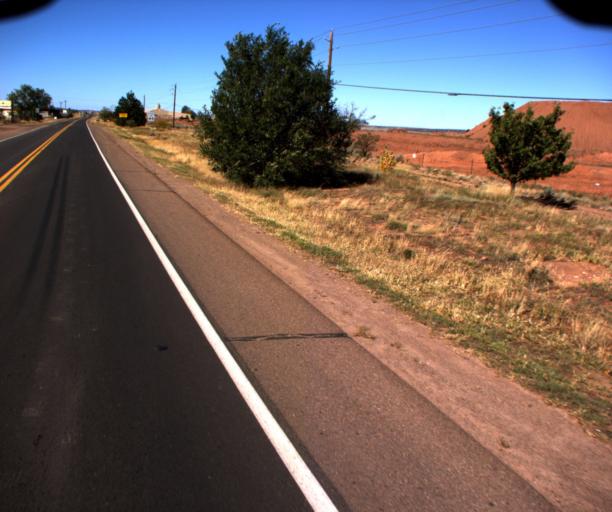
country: US
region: Arizona
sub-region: Navajo County
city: Snowflake
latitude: 34.5134
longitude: -110.0887
